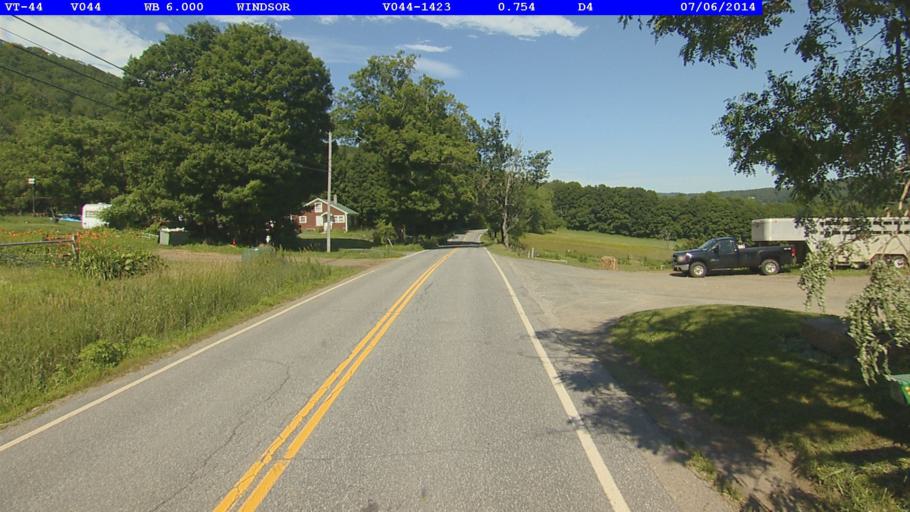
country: US
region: Vermont
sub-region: Windsor County
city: Windsor
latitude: 43.4655
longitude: -72.4384
